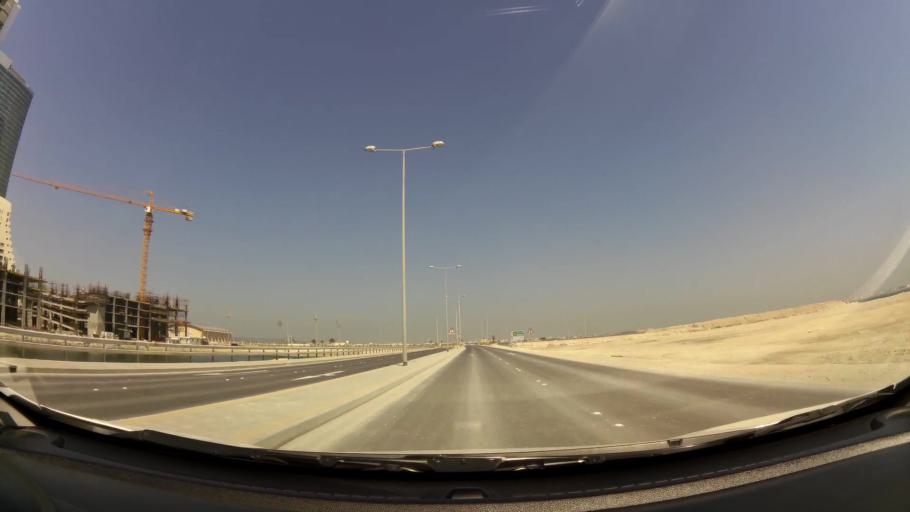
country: BH
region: Manama
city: Manama
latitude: 26.2225
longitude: 50.6126
